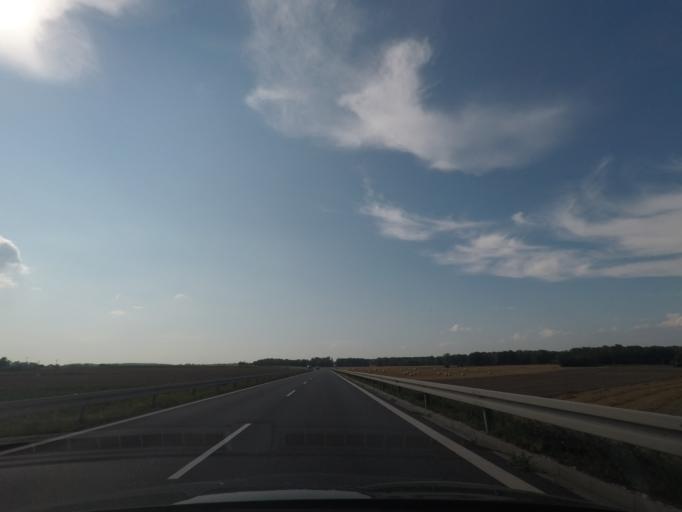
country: PL
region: Silesian Voivodeship
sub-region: Powiat pszczynski
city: Piasek
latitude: 49.9994
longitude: 18.9381
